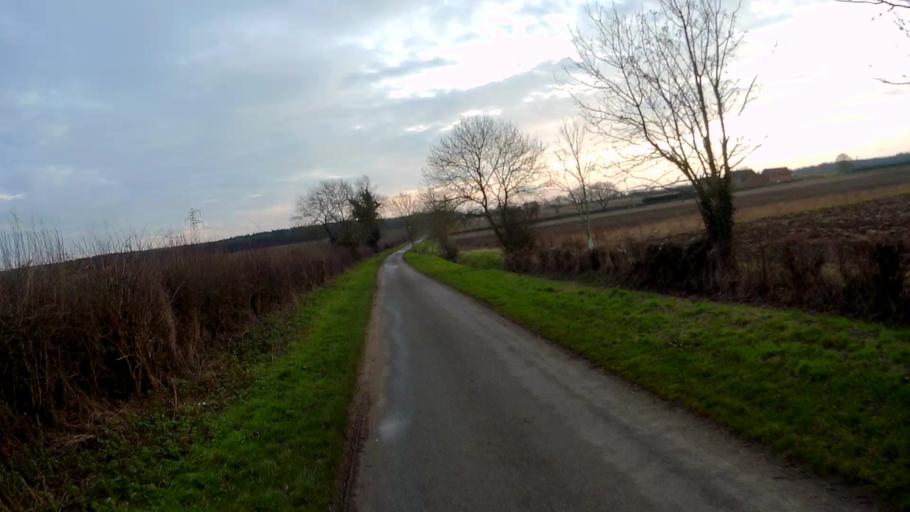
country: GB
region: England
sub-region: Lincolnshire
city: Bourne
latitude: 52.8285
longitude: -0.4055
